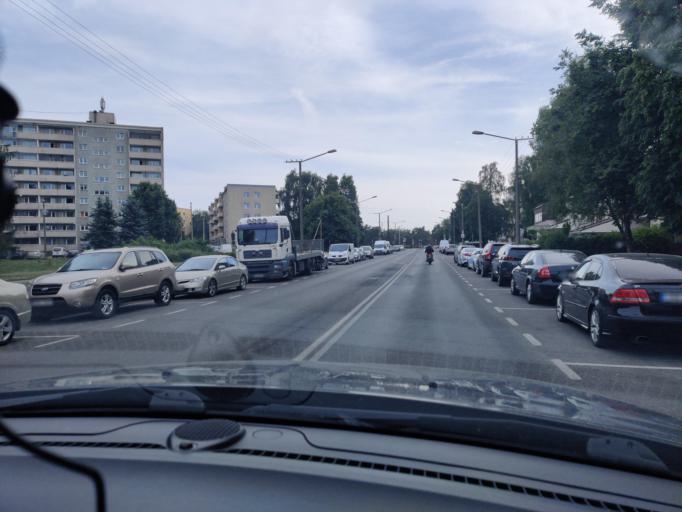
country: EE
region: Harju
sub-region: Tallinna linn
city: Tallinn
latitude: 59.4031
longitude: 24.6793
